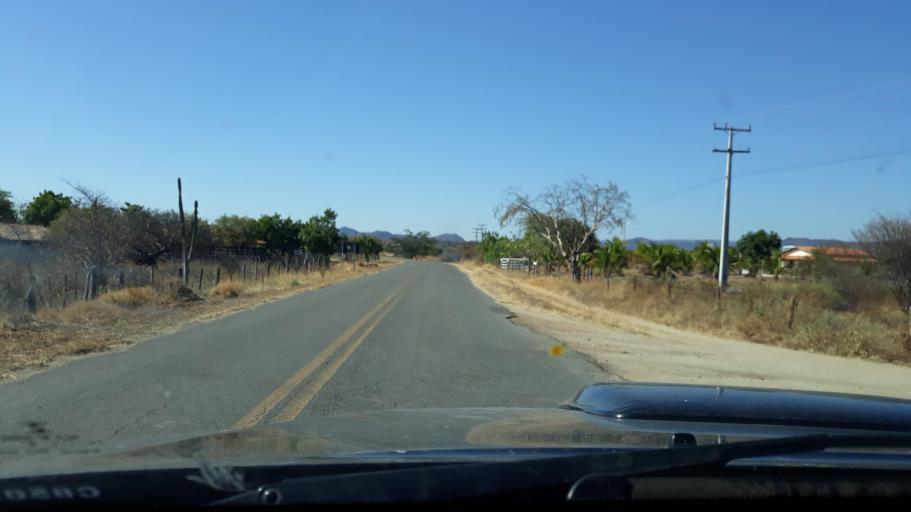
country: BR
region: Bahia
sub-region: Guanambi
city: Guanambi
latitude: -14.0193
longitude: -42.8648
